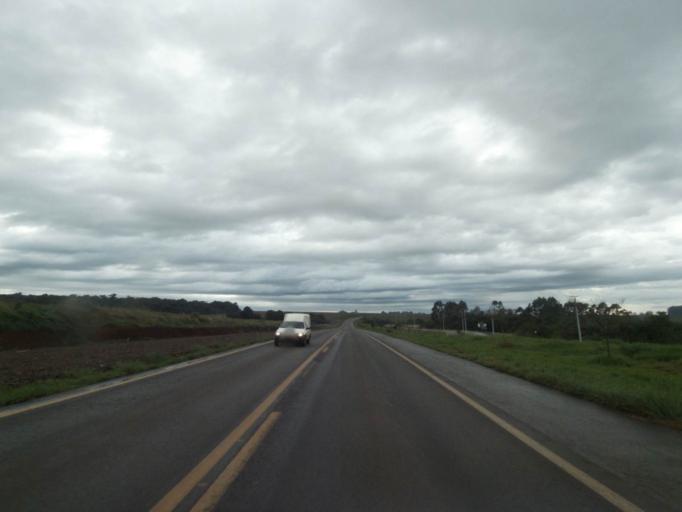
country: BR
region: Parana
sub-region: Toledo
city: Toledo
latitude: -24.6896
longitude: -53.7561
